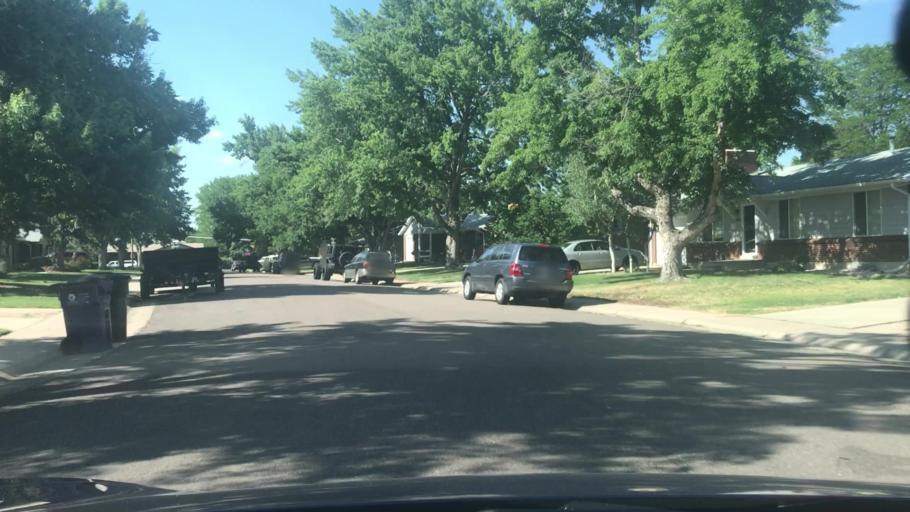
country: US
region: Colorado
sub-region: Arapahoe County
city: Glendale
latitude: 39.6912
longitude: -104.9104
